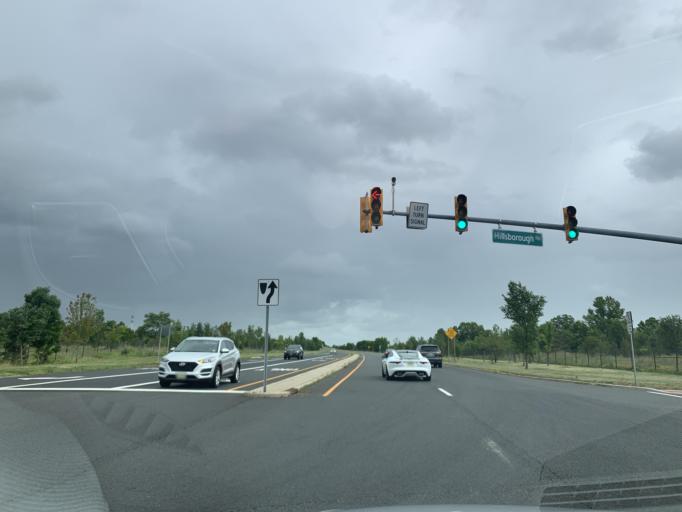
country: US
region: New Jersey
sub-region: Somerset County
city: Bloomingdale
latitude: 40.4805
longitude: -74.6440
